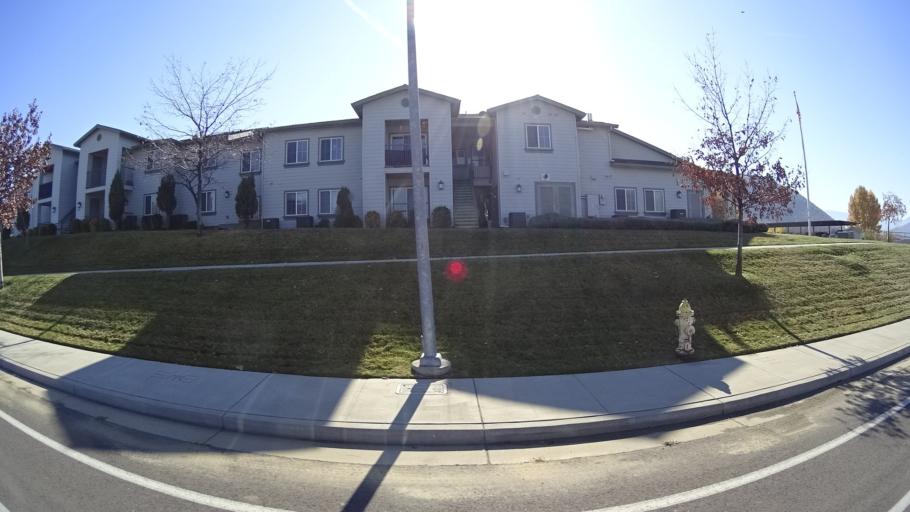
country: US
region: California
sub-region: Siskiyou County
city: Yreka
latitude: 41.7339
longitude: -122.6275
